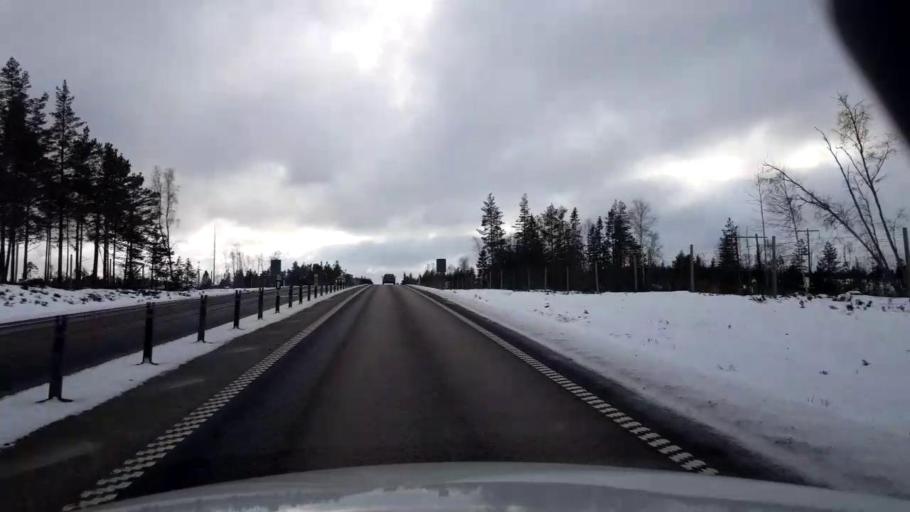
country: SE
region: Gaevleborg
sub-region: Hudiksvalls Kommun
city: Hudiksvall
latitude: 61.8196
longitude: 17.1905
